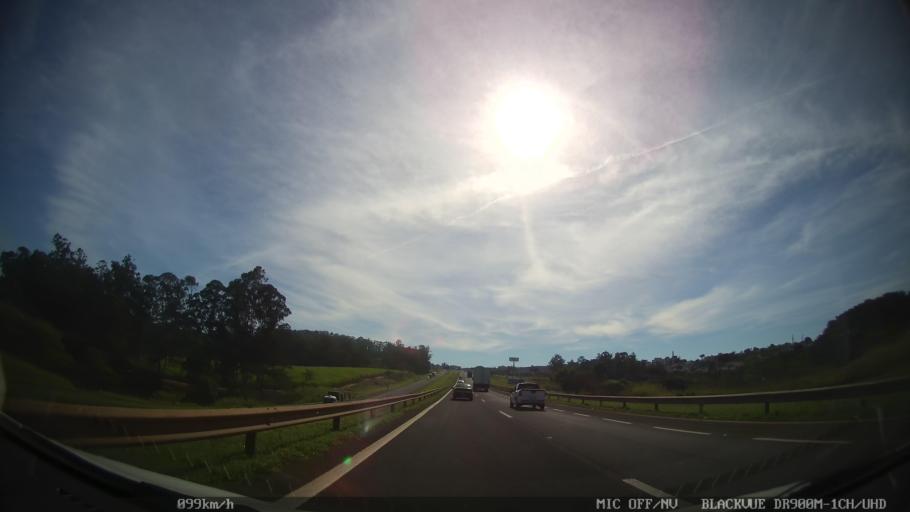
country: BR
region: Sao Paulo
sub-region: Araras
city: Araras
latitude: -22.3417
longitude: -47.3922
